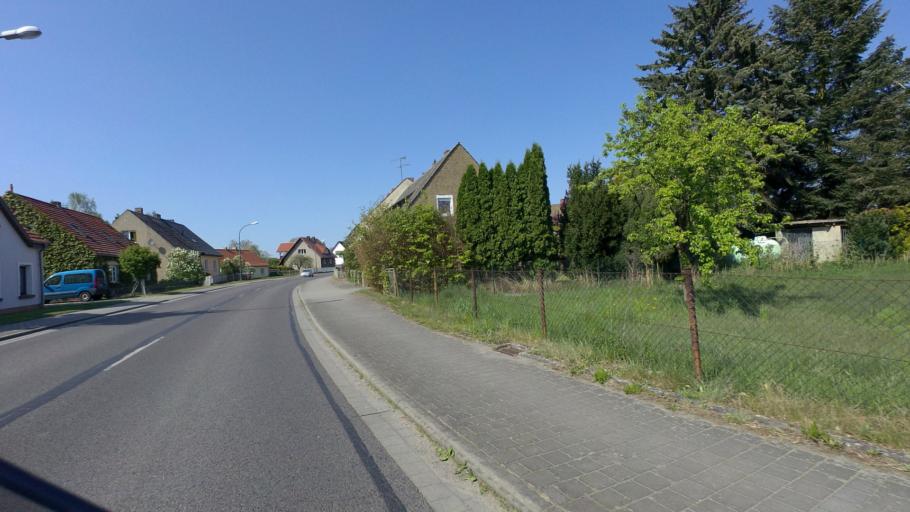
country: DE
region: Brandenburg
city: Schlepzig
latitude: 52.0719
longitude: 13.8944
